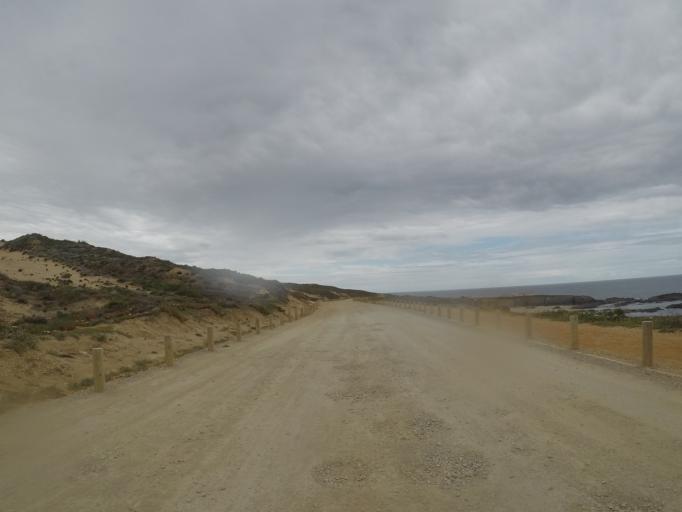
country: PT
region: Beja
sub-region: Odemira
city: Vila Nova de Milfontes
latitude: 37.6504
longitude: -8.8022
